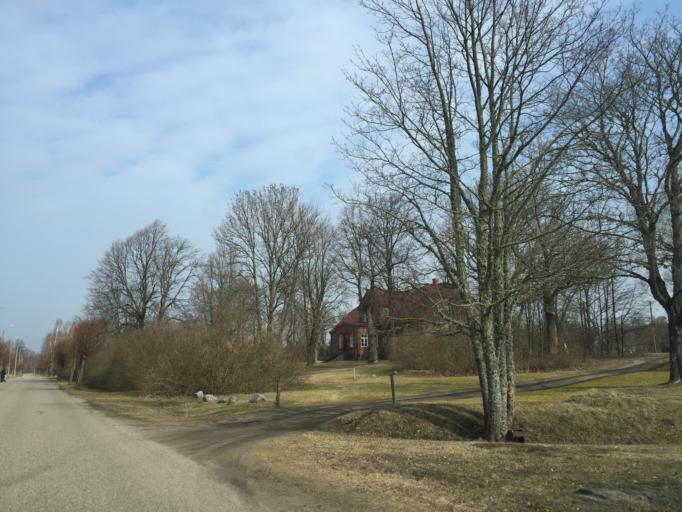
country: LV
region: Salacgrivas
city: Ainazi
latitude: 57.8663
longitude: 24.3595
